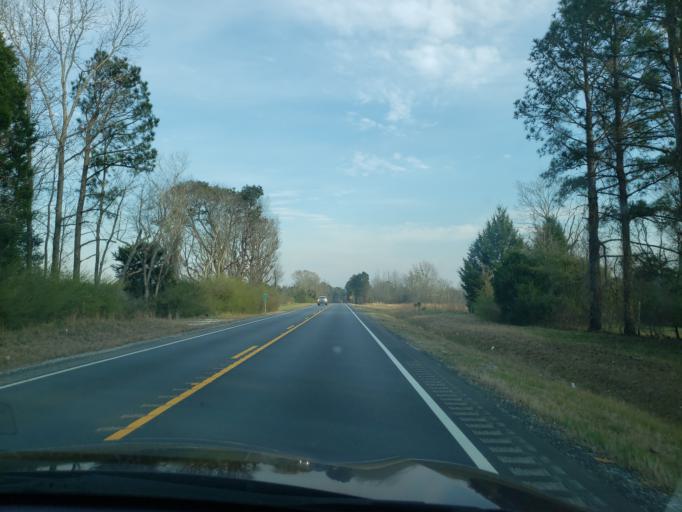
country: US
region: Alabama
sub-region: Hale County
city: Moundville
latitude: 32.8933
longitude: -87.6172
